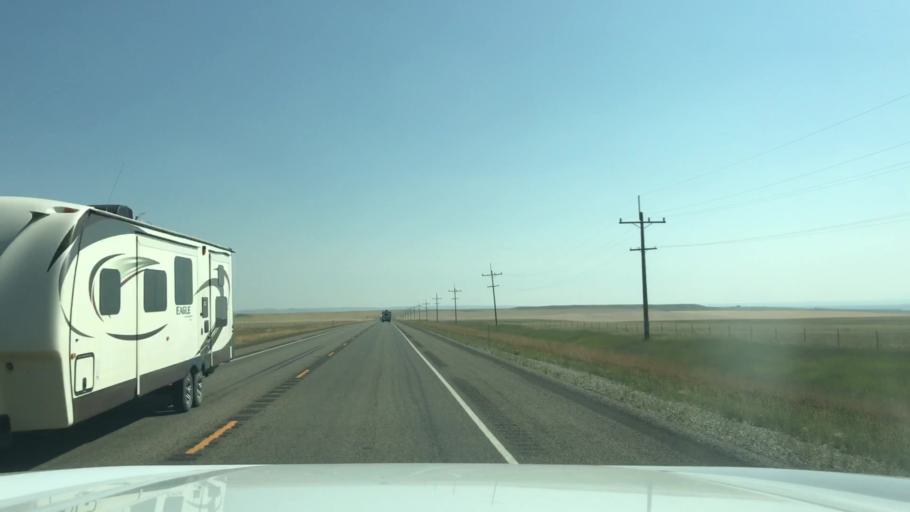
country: US
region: Montana
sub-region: Wheatland County
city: Harlowton
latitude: 46.5015
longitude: -109.7660
